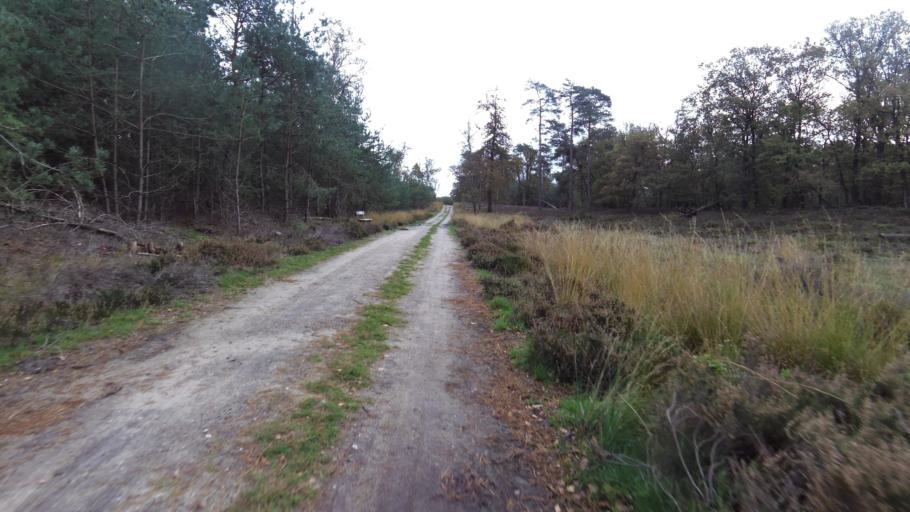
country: NL
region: Gelderland
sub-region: Gemeente Apeldoorn
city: Uddel
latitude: 52.3052
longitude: 5.8374
